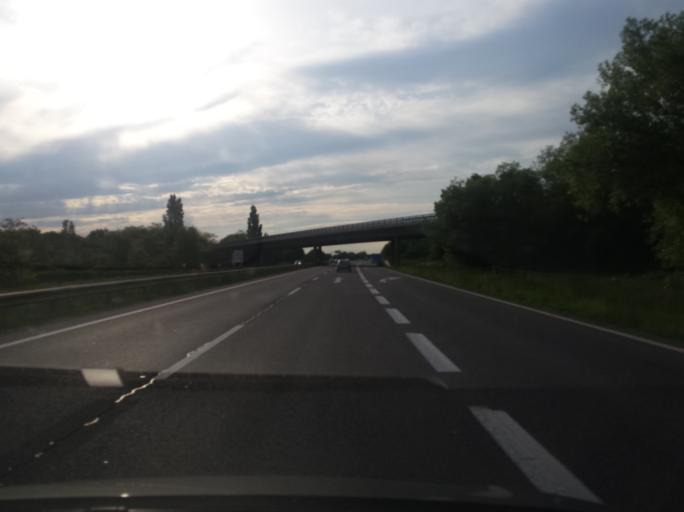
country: AT
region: Burgenland
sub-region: Eisenstadt-Umgebung
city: Mullendorf
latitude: 47.8316
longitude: 16.4578
